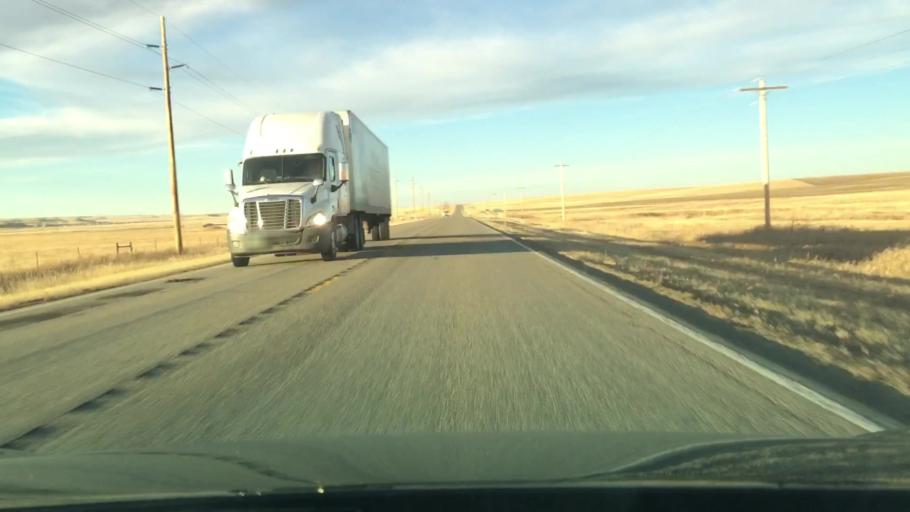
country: US
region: Montana
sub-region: Wheatland County
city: Harlowton
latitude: 46.8205
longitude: -109.7606
